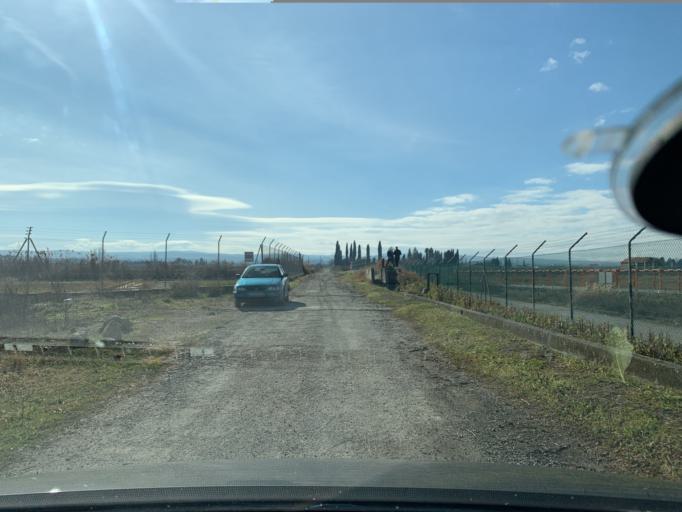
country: ES
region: Andalusia
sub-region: Provincia de Granada
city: Chauchina
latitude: 37.1892
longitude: -3.7577
